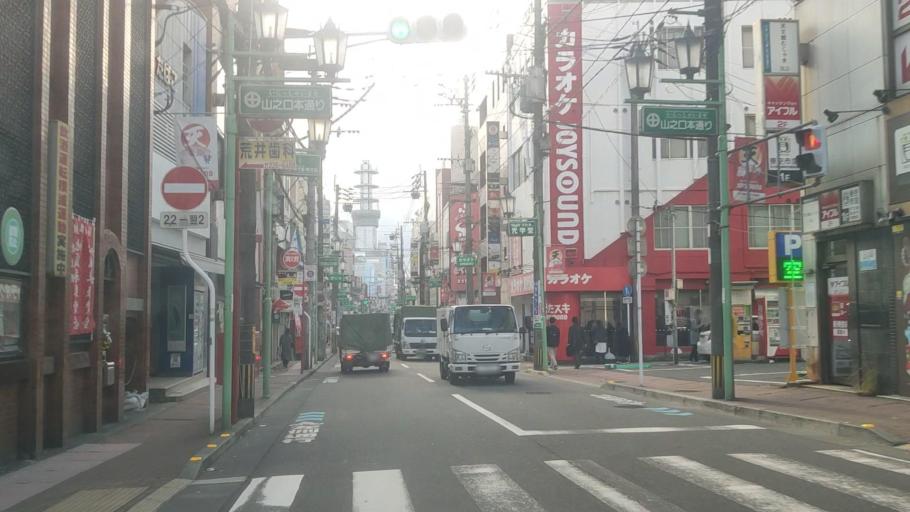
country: JP
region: Kagoshima
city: Kagoshima-shi
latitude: 31.5892
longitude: 130.5574
